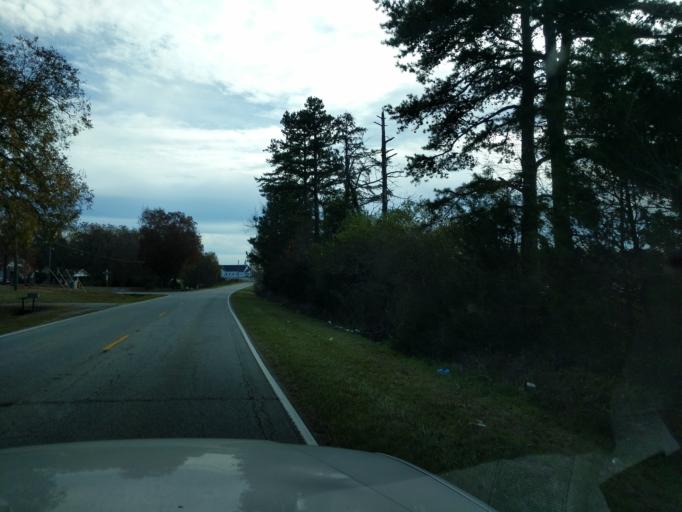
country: US
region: South Carolina
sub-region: Spartanburg County
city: Woodruff
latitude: 34.6931
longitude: -81.9959
